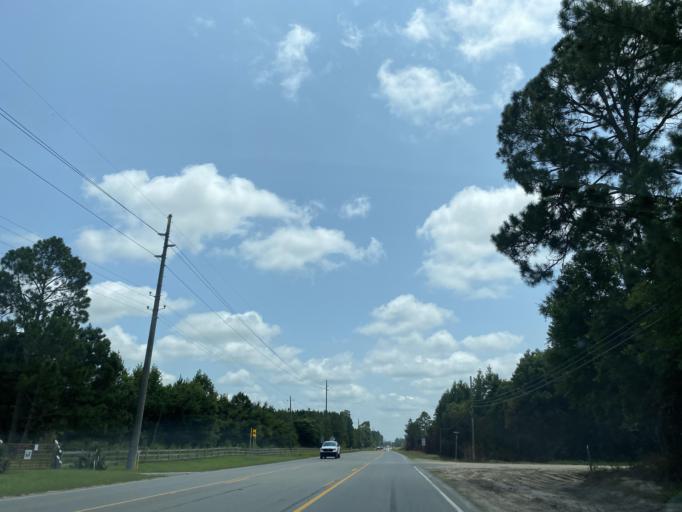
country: US
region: Georgia
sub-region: Jeff Davis County
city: Hazlehurst
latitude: 31.8391
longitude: -82.5819
